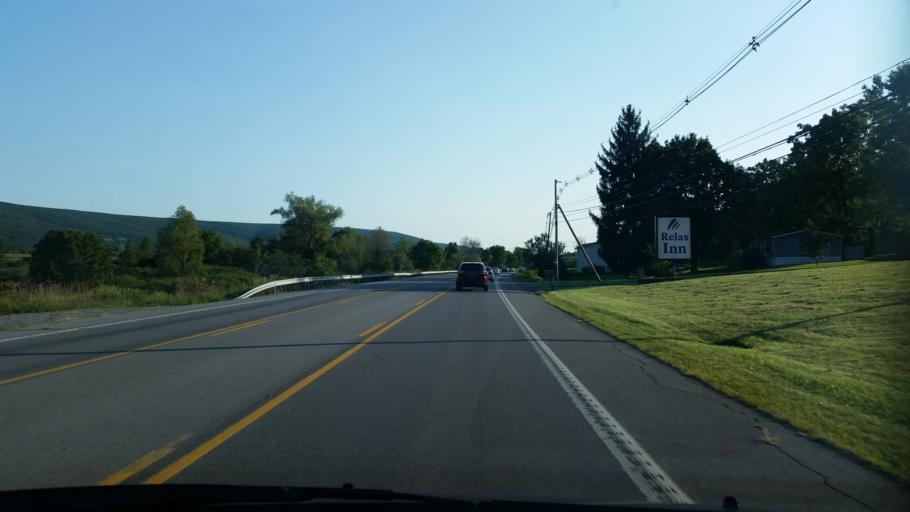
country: US
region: Pennsylvania
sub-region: Blair County
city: Bellwood
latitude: 40.5859
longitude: -78.3255
